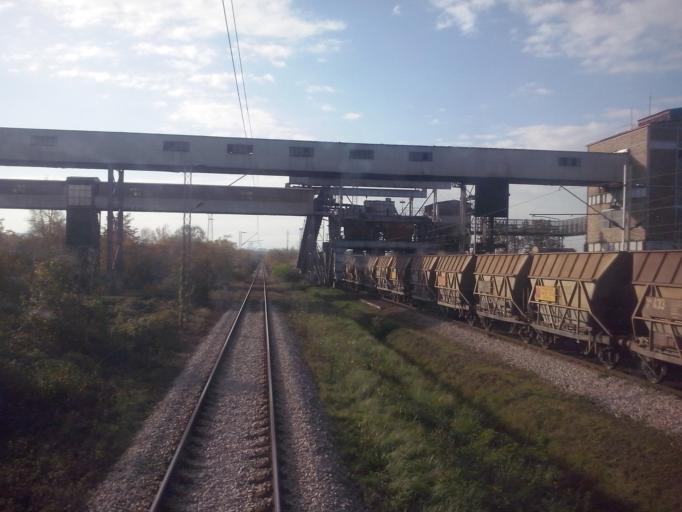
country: RS
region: Central Serbia
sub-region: Belgrade
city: Lazarevac
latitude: 44.4298
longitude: 20.2769
